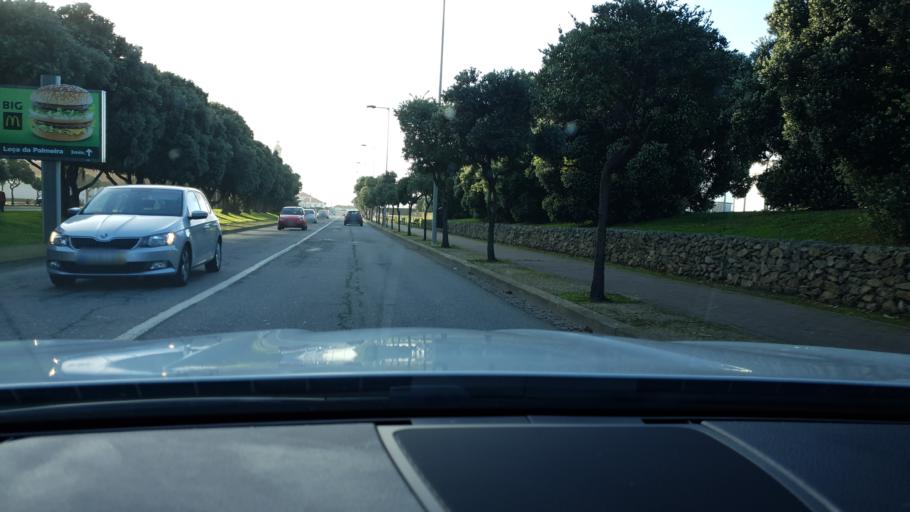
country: PT
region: Porto
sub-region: Matosinhos
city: Leca da Palmeira
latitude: 41.2014
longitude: -8.7059
